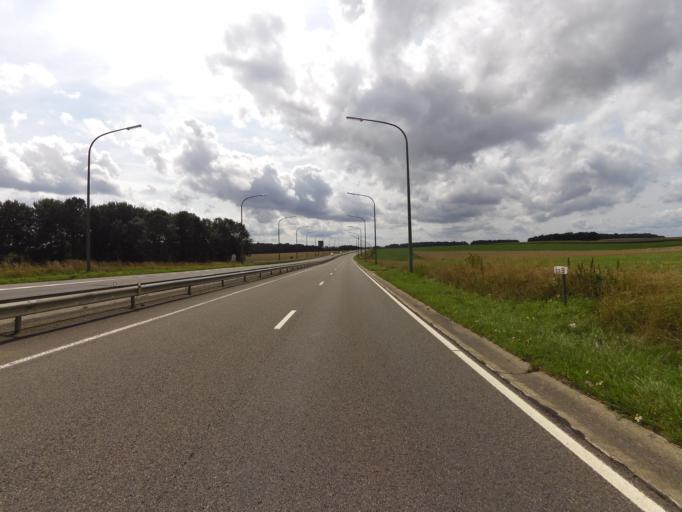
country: BE
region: Wallonia
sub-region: Province de Liege
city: Tinlot
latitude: 50.4682
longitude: 5.3692
